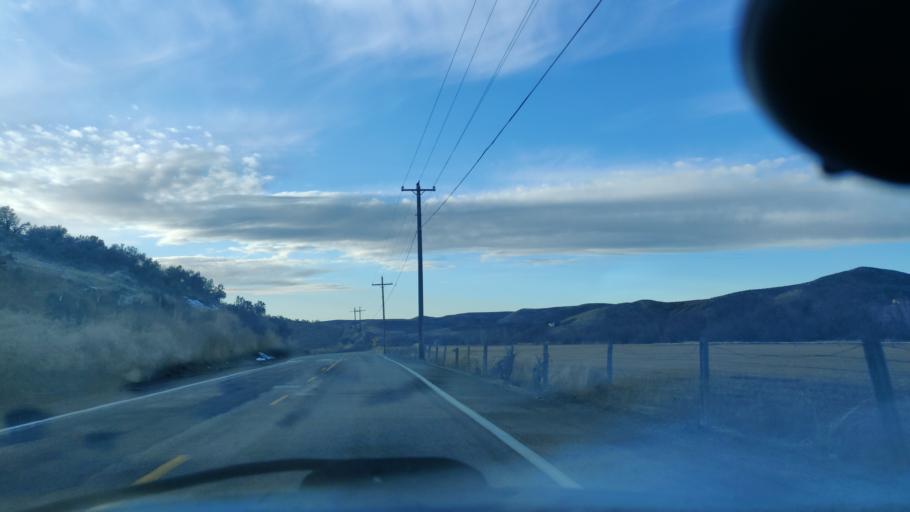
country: US
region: Idaho
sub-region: Ada County
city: Eagle
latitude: 43.7301
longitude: -116.2944
